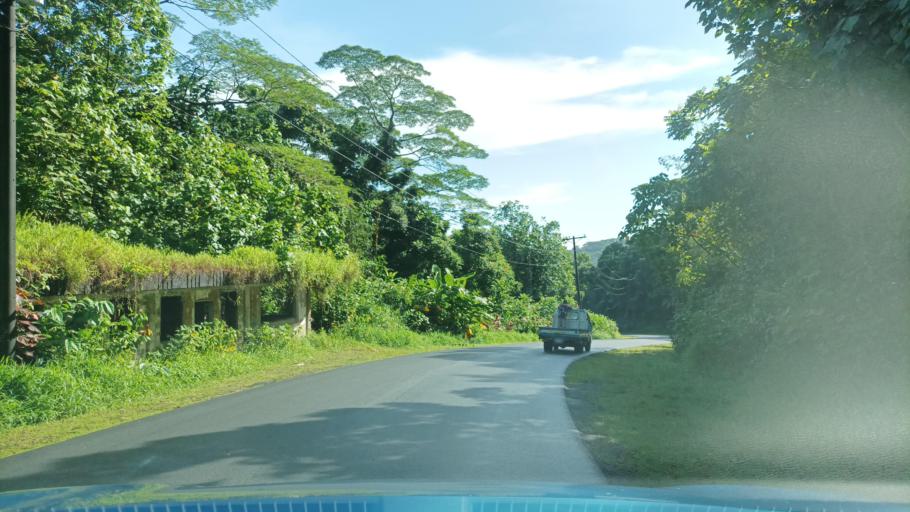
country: FM
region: Pohnpei
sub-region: Sokehs Municipality
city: Palikir - National Government Center
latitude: 6.9262
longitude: 158.1749
